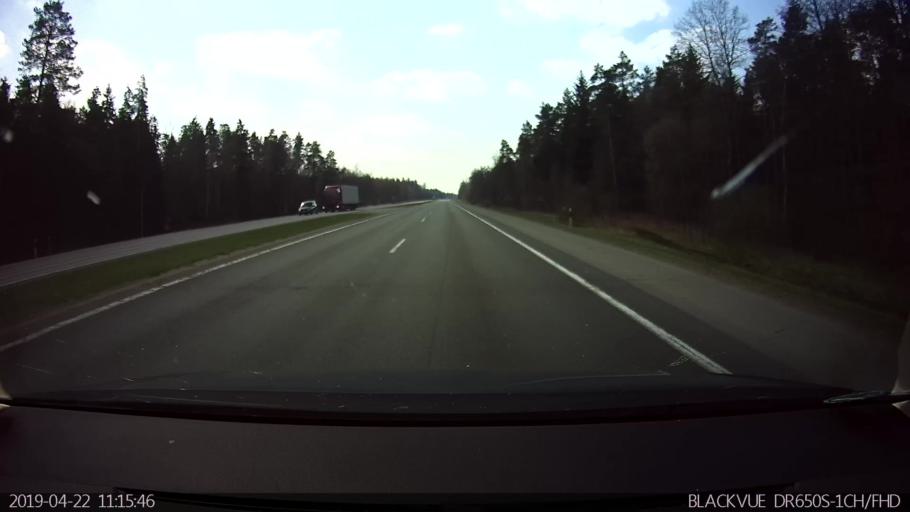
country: BY
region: Minsk
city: Horad Barysaw
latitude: 54.1620
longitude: 28.5643
